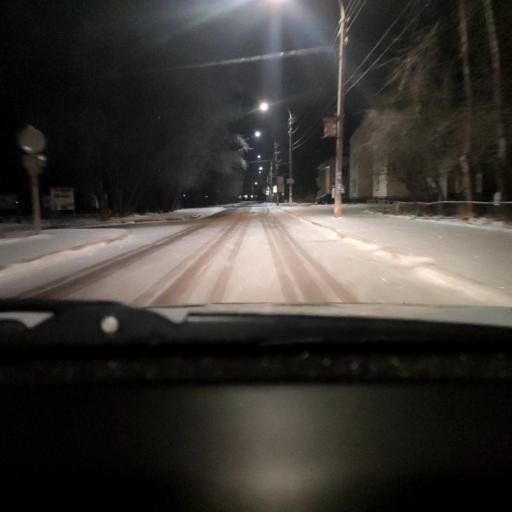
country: RU
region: Perm
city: Ust'-Kachka
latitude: 58.0049
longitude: 55.6720
